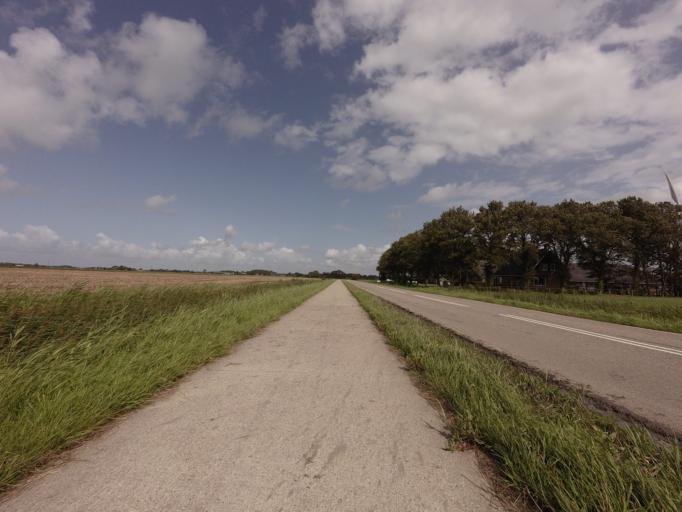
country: NL
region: Friesland
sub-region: Gemeente Harlingen
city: Harlingen
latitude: 53.1395
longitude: 5.4744
